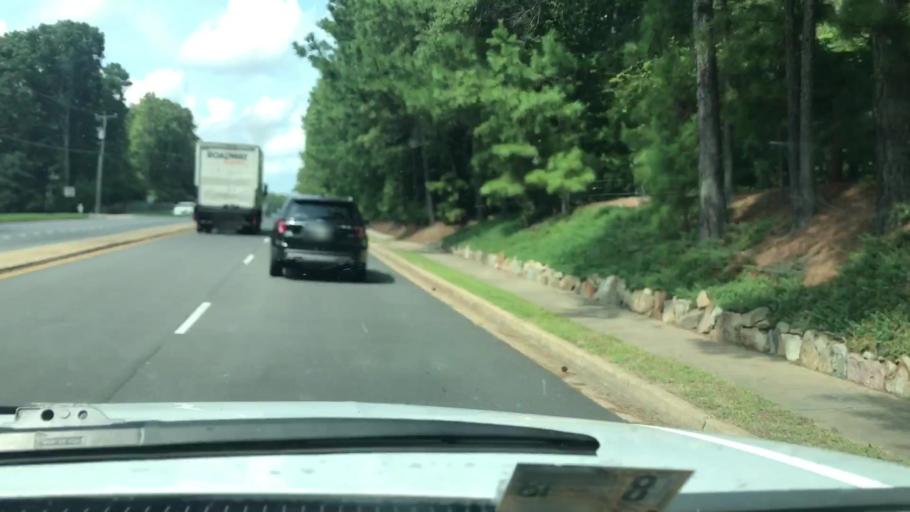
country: US
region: Virginia
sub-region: Henrico County
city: Short Pump
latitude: 37.6077
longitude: -77.6067
